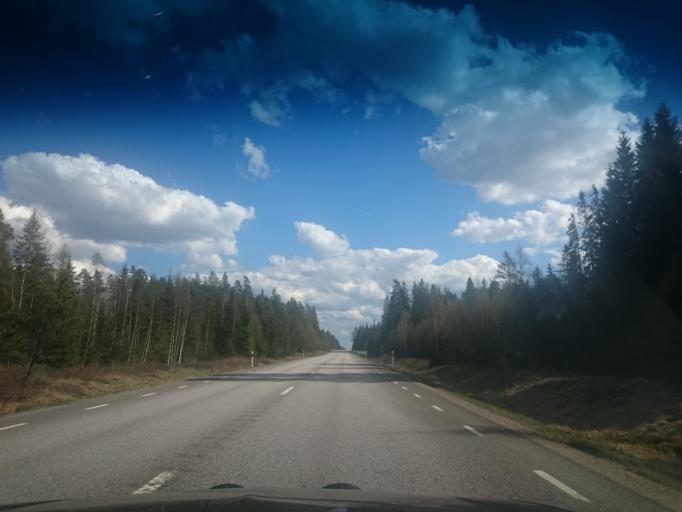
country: SE
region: Joenkoeping
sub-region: Vetlanda Kommun
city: Vetlanda
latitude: 57.2519
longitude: 15.1337
